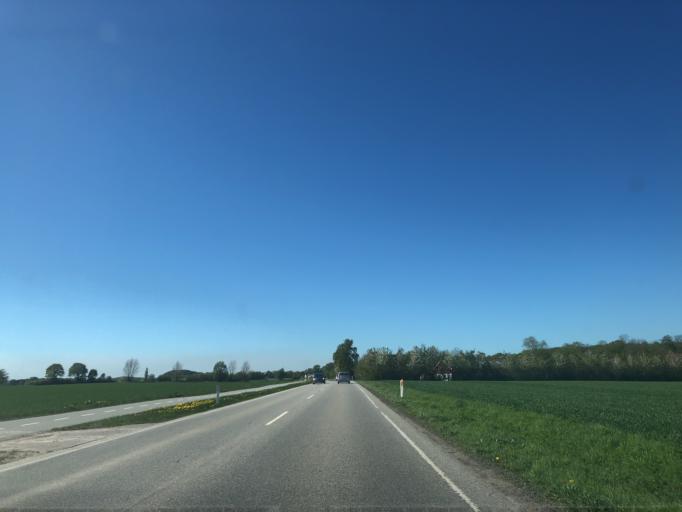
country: DK
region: Zealand
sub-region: Stevns Kommune
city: Store Heddinge
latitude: 55.3367
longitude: 12.3493
